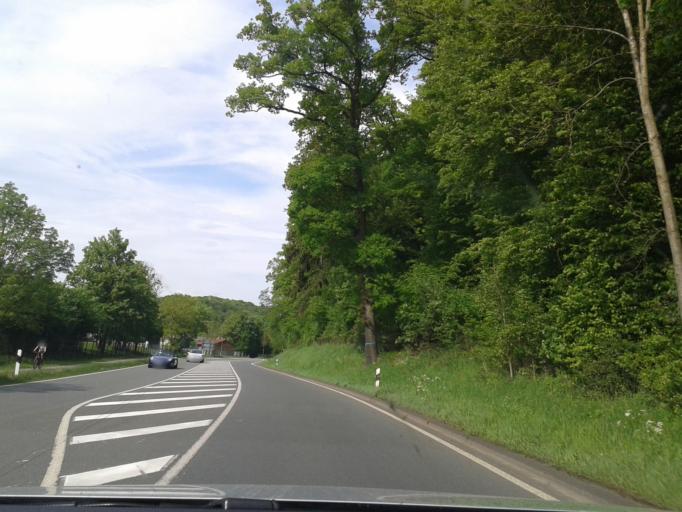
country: DE
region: Hesse
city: Frankenberg
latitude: 51.0780
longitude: 8.8217
